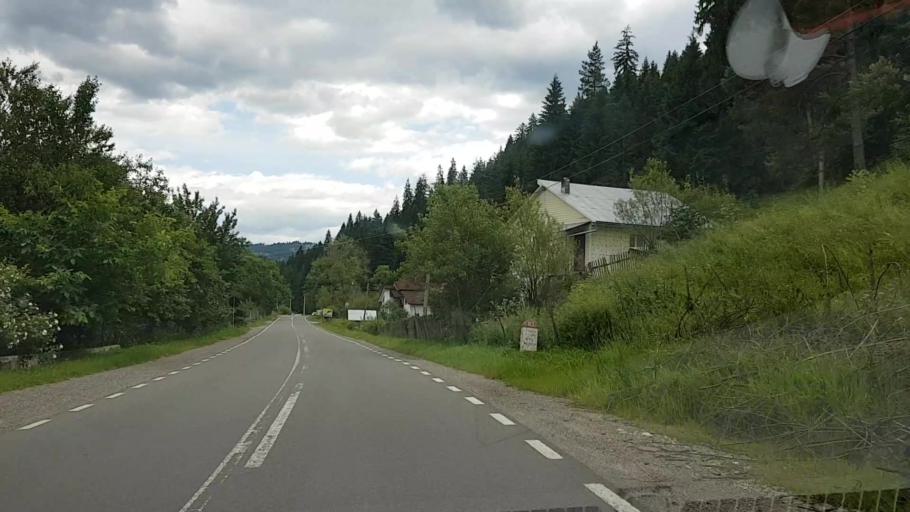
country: RO
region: Neamt
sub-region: Comuna Poiana Teiului
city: Poiana Teiului
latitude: 47.1072
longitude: 25.9323
